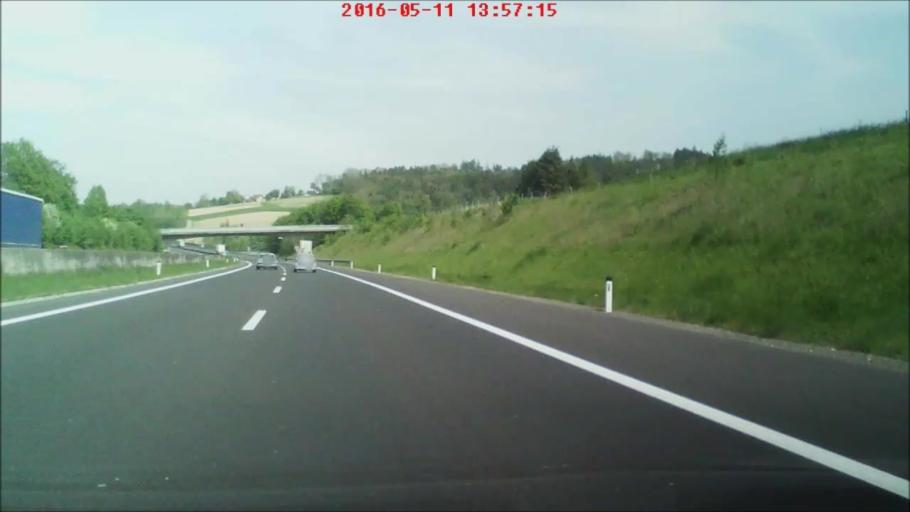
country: AT
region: Upper Austria
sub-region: Wels-Land
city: Pennewang
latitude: 48.1781
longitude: 13.8860
